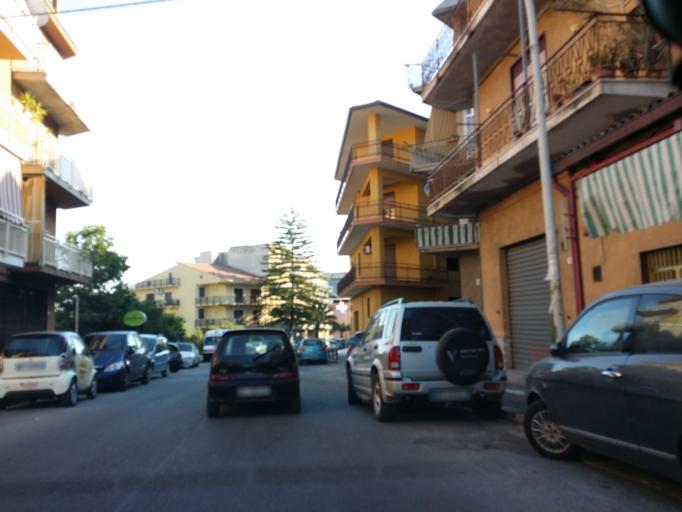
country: IT
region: Sicily
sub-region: Palermo
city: Misilmeri
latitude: 38.0381
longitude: 13.4586
